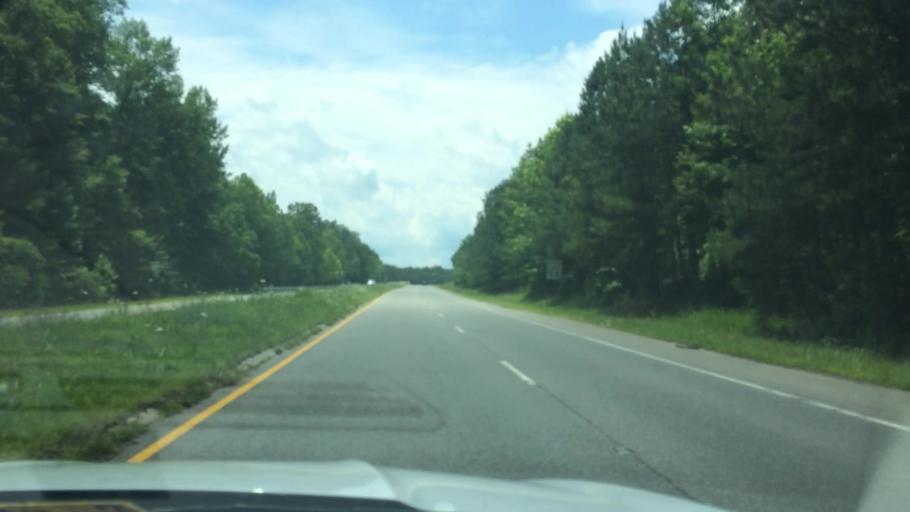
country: US
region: Virginia
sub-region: Middlesex County
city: Saluda
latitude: 37.5642
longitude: -76.6182
